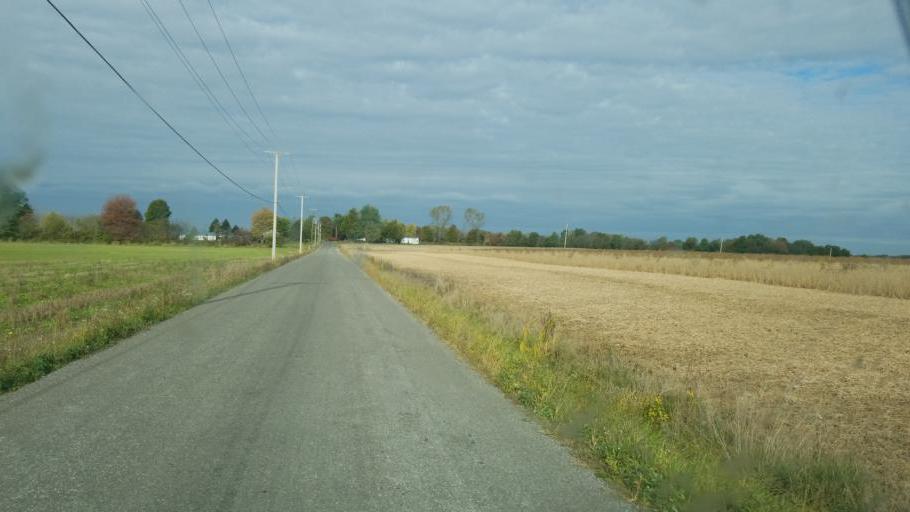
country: US
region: Pennsylvania
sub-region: Mercer County
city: Reynolds Heights
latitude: 41.3282
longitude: -80.2945
